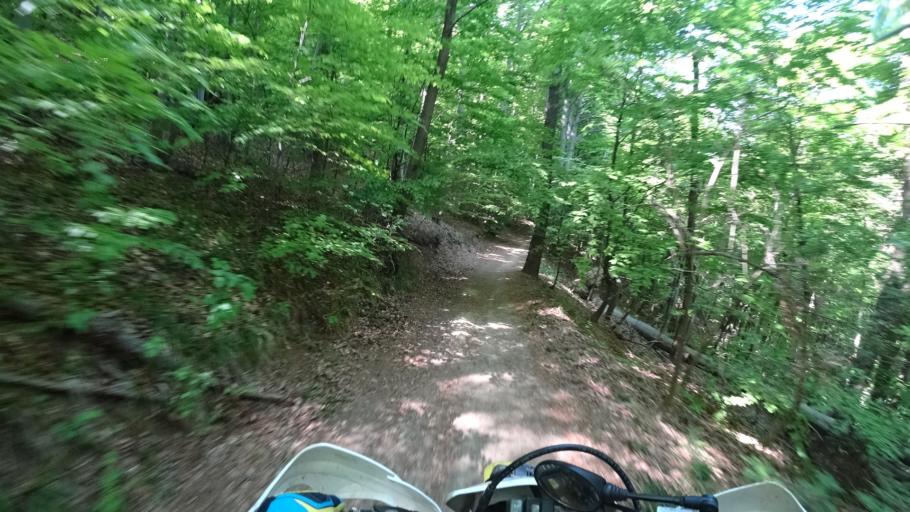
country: HR
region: Zagrebacka
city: Jablanovec
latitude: 45.8759
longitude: 15.8966
